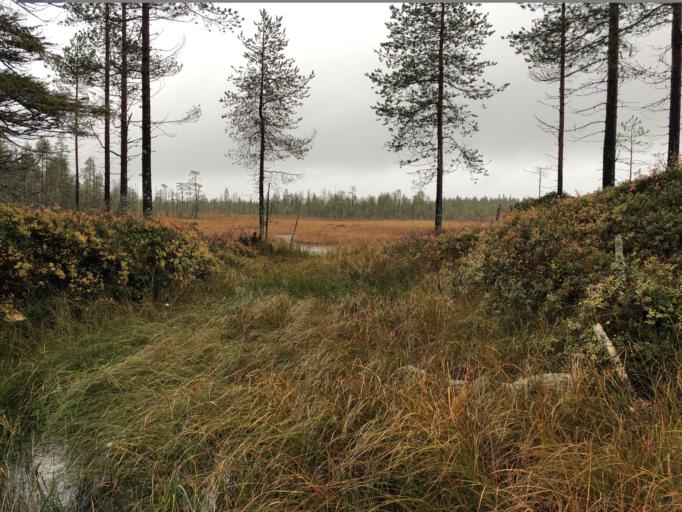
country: FI
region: Lapland
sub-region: Itae-Lappi
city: Posio
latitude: 65.9931
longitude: 28.5478
